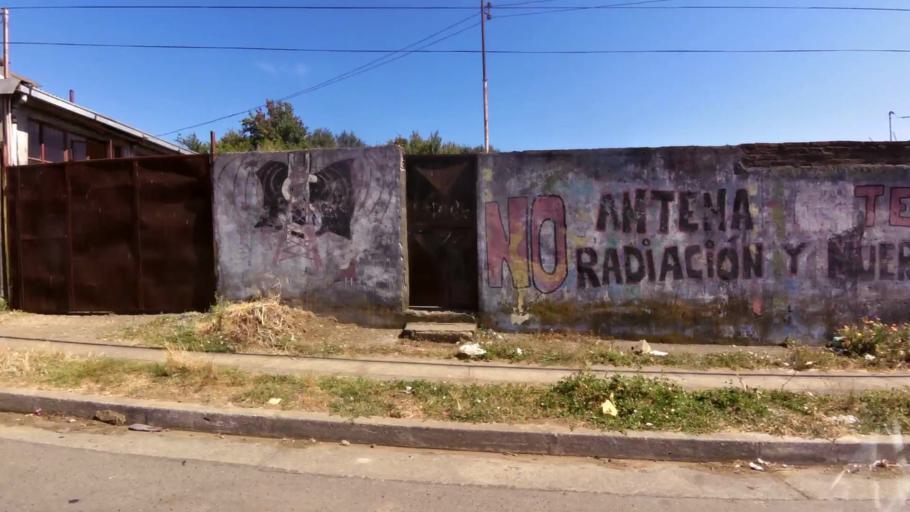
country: CL
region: Biobio
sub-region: Provincia de Concepcion
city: Penco
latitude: -36.7272
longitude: -72.9879
